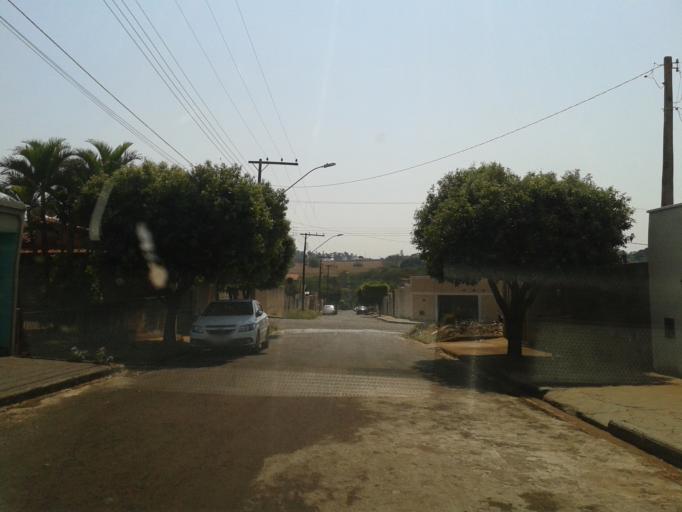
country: BR
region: Minas Gerais
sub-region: Ituiutaba
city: Ituiutaba
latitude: -18.9701
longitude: -49.4805
